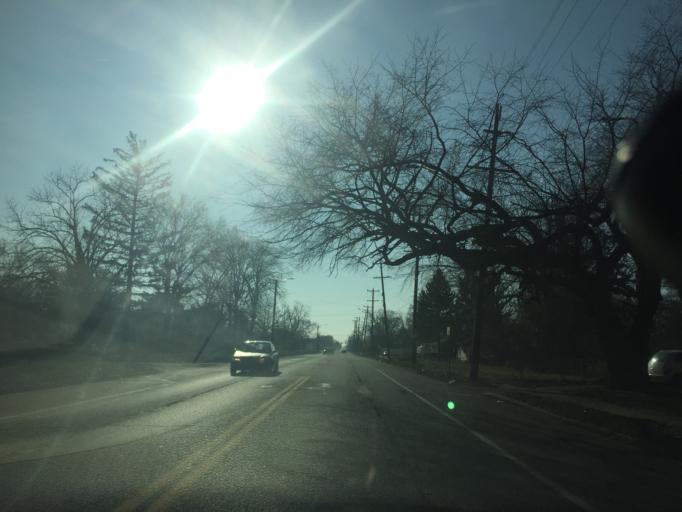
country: US
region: Michigan
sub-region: Macomb County
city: Eastpointe
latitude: 42.4393
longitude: -82.9656
